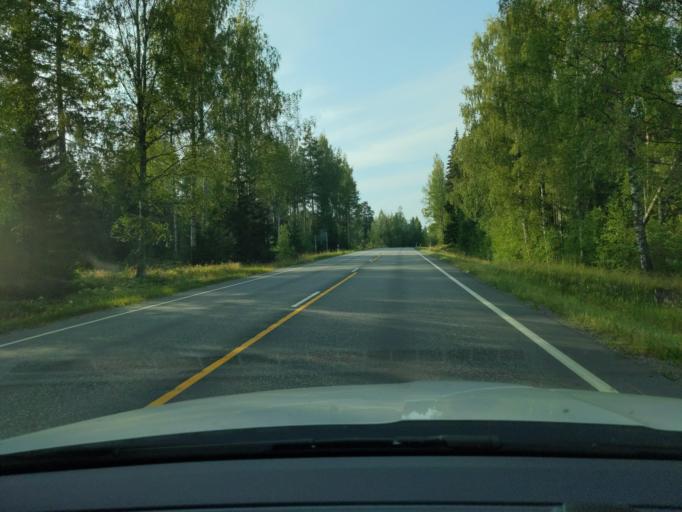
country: FI
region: Paijanne Tavastia
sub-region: Lahti
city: Padasjoki
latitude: 61.3066
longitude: 25.2945
